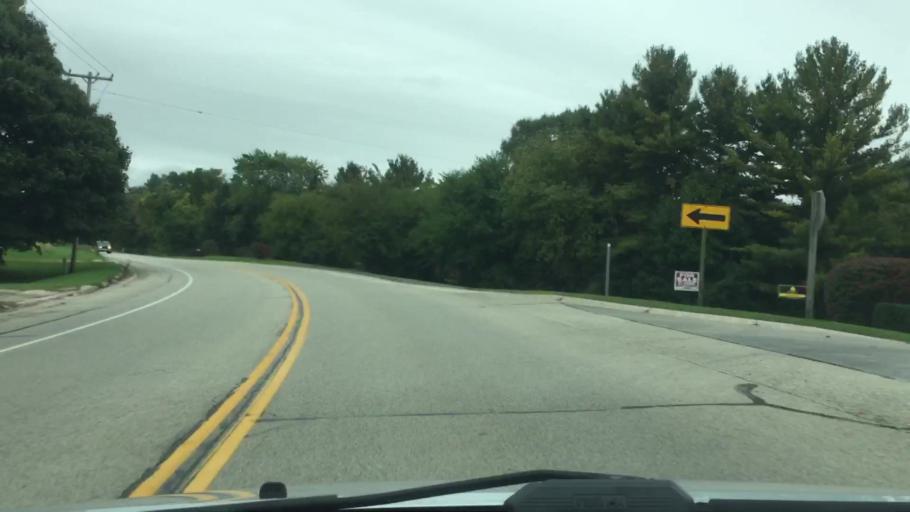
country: US
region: Wisconsin
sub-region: Jefferson County
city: Palmyra
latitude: 42.7888
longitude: -88.5631
